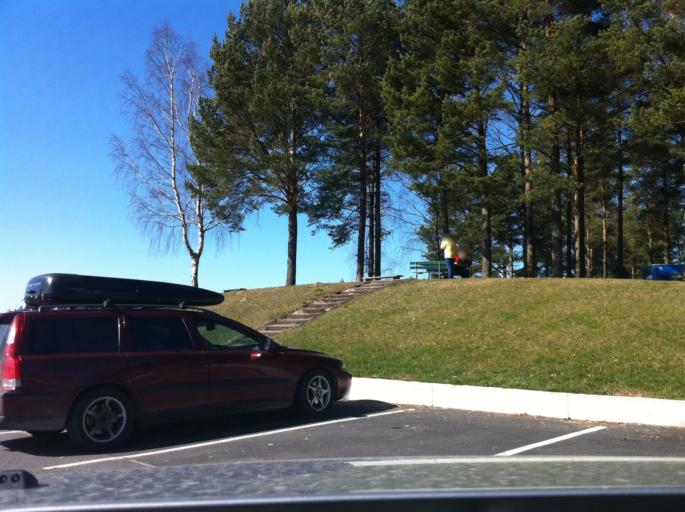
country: SE
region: Joenkoeping
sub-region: Jonkopings Kommun
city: Odensjo
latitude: 57.6669
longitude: 14.1819
